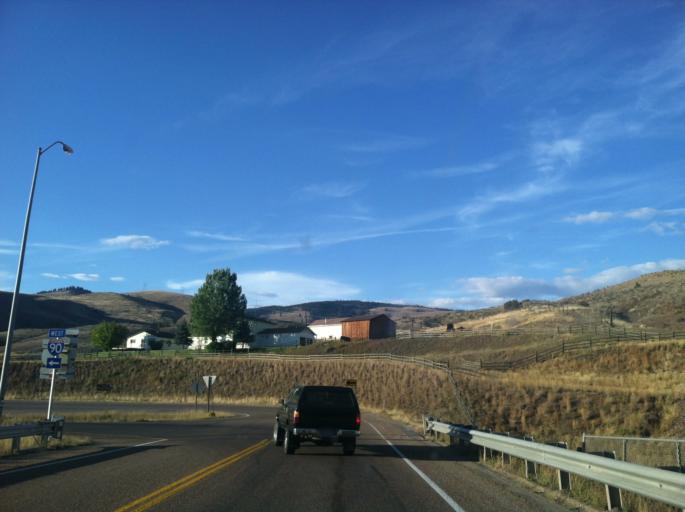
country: US
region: Montana
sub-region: Granite County
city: Philipsburg
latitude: 46.6723
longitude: -113.1538
